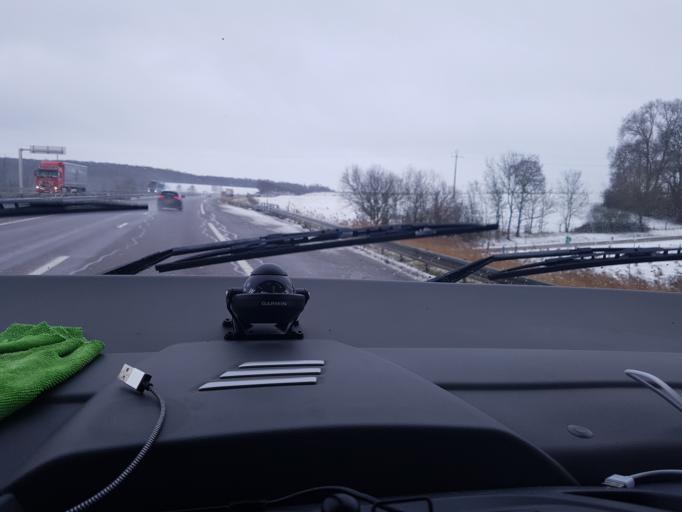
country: FR
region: Lorraine
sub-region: Departement de la Moselle
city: Argancy
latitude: 49.1814
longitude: 6.2451
